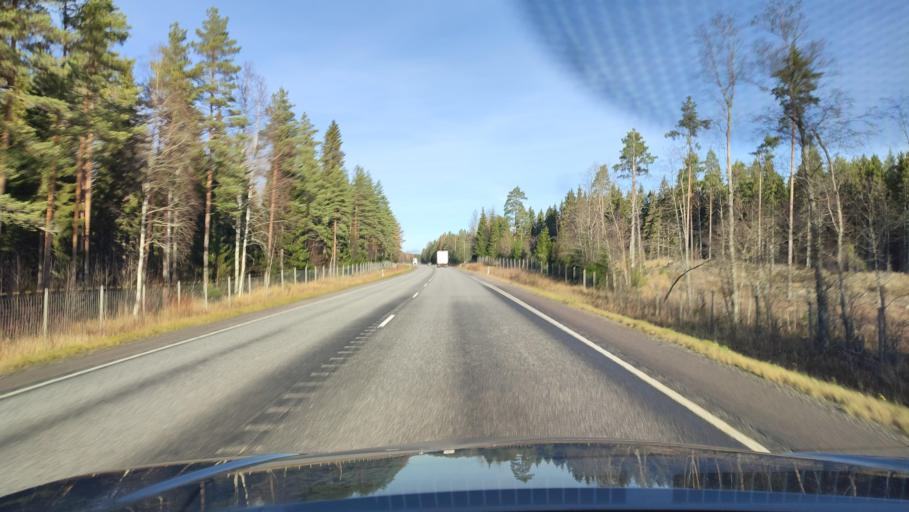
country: FI
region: Ostrobothnia
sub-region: Vaasa
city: Malax
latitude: 62.8367
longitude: 21.6959
